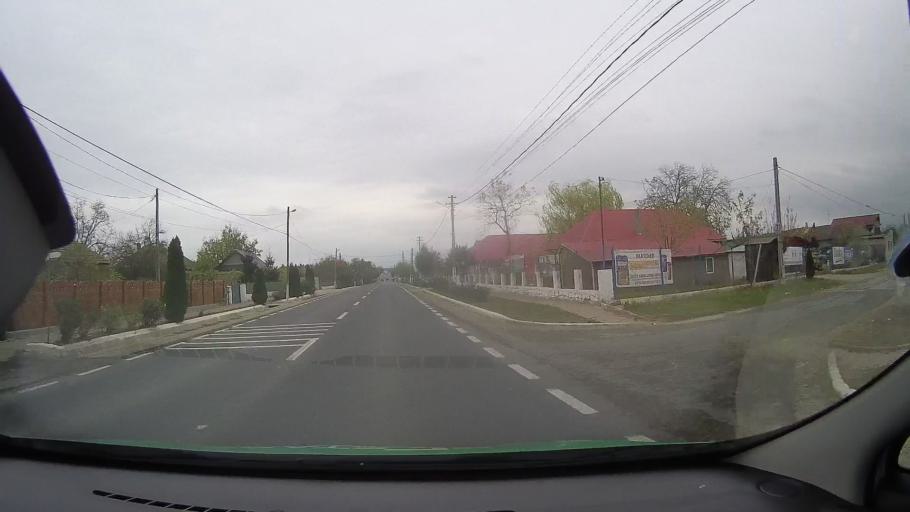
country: RO
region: Constanta
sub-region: Comuna Nicolae Balcescu
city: Nicolae Balcescu
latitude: 44.3889
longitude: 28.3741
